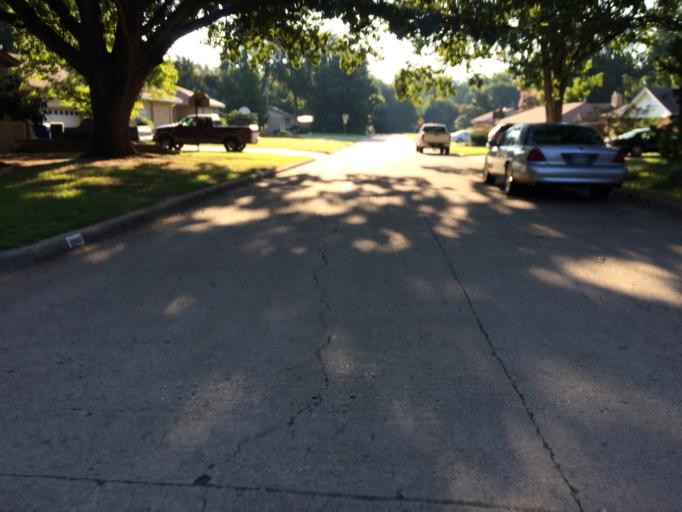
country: US
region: Oklahoma
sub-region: Cleveland County
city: Norman
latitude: 35.2094
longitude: -97.4581
